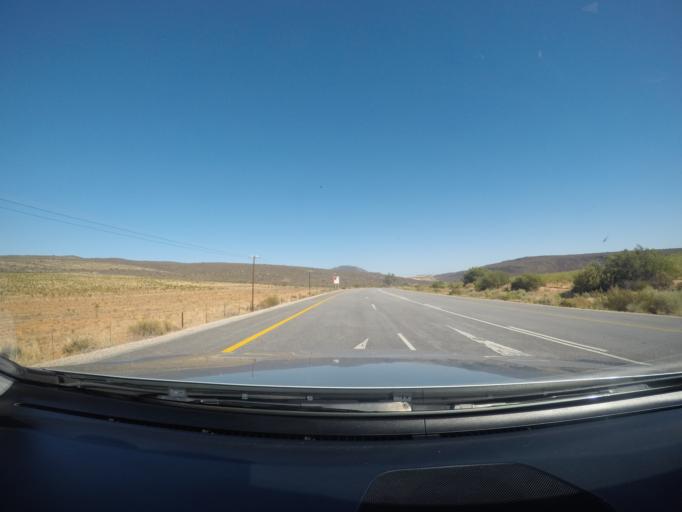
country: ZA
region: Western Cape
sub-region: West Coast District Municipality
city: Clanwilliam
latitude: -32.3207
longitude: 18.9146
